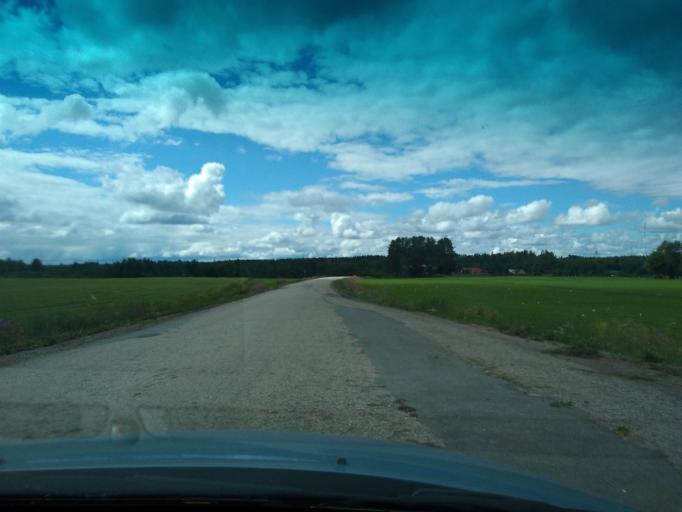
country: FI
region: Central Finland
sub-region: Saarijaervi-Viitasaari
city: Saarijaervi
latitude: 62.8121
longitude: 25.0345
